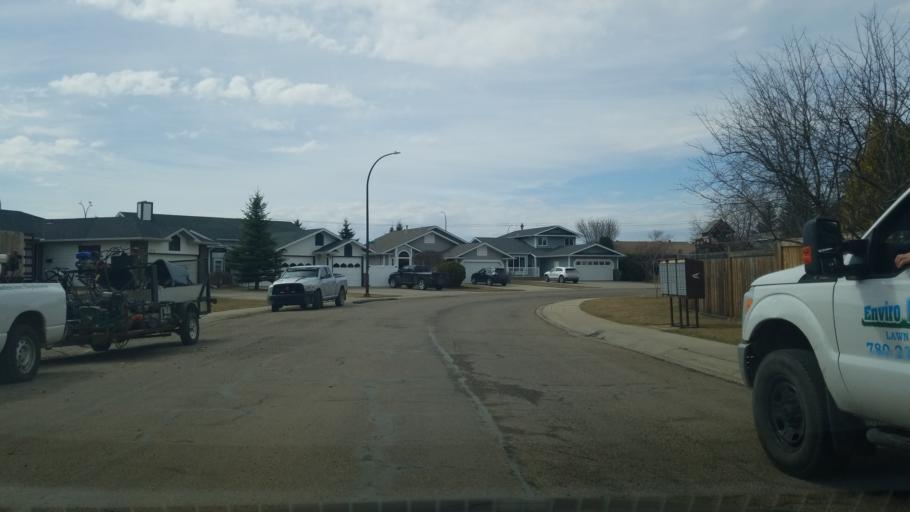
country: CA
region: Saskatchewan
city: Lloydminster
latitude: 53.2713
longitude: -110.0280
